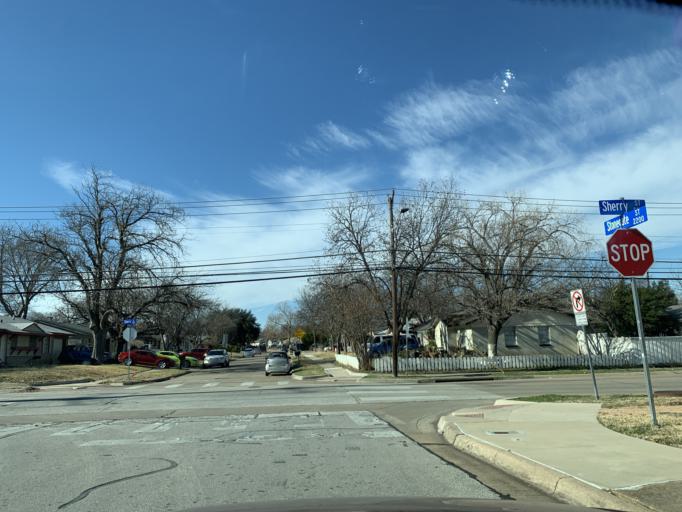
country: US
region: Texas
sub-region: Tarrant County
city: Arlington
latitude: 32.7258
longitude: -97.0715
